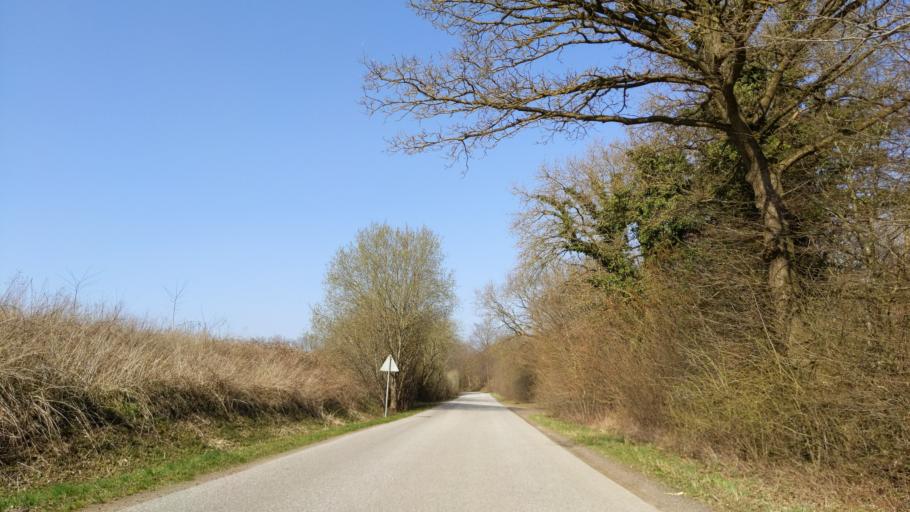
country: DE
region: Schleswig-Holstein
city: Susel
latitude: 54.0902
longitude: 10.7130
